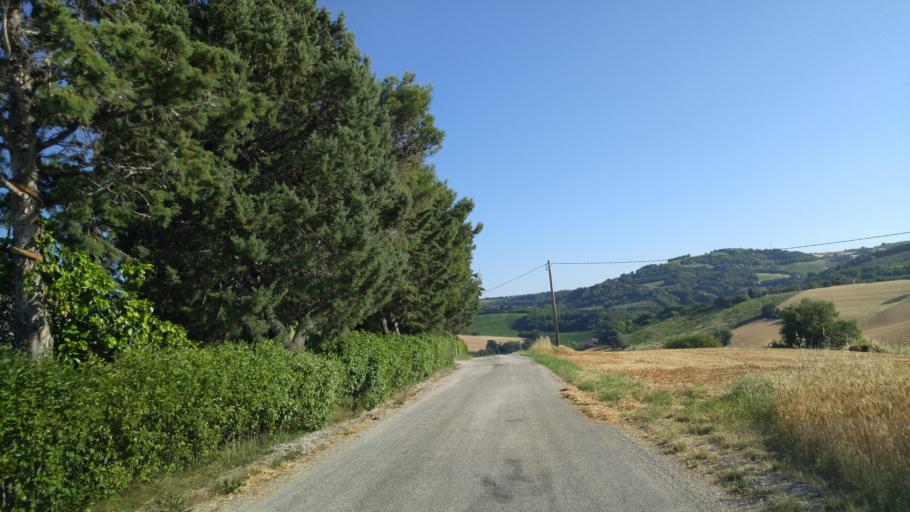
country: IT
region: The Marches
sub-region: Provincia di Pesaro e Urbino
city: Cartoceto
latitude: 43.7949
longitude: 12.8854
